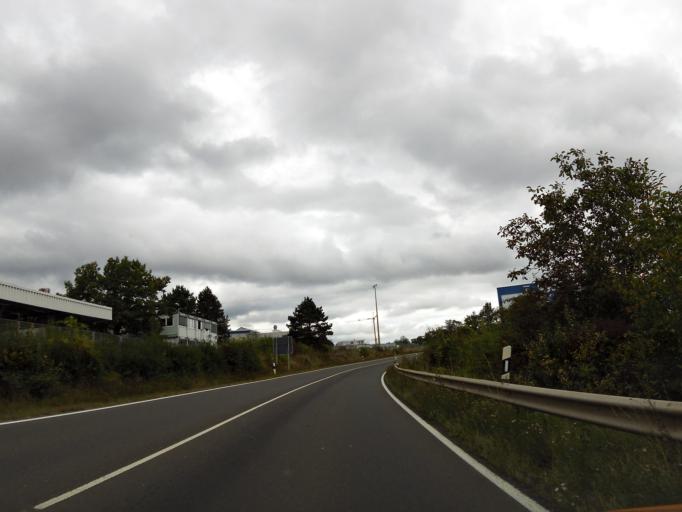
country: DE
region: Rheinland-Pfalz
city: Kirchheimbolanden
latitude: 49.6546
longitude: 8.0201
